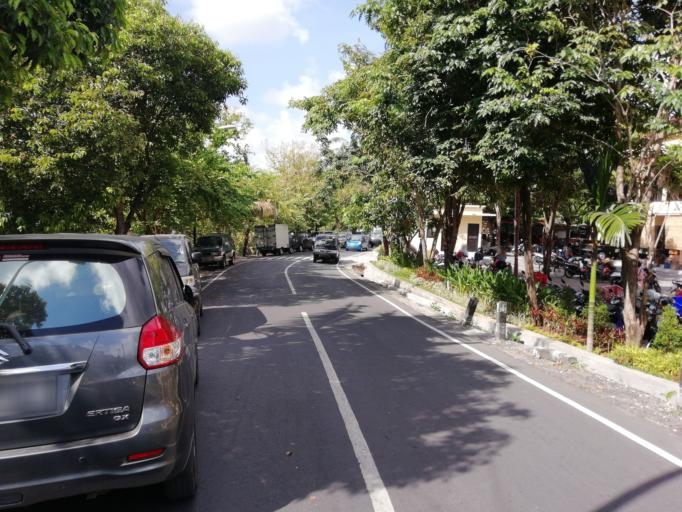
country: ID
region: Bali
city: Kuta
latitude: -8.6983
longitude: 115.1722
